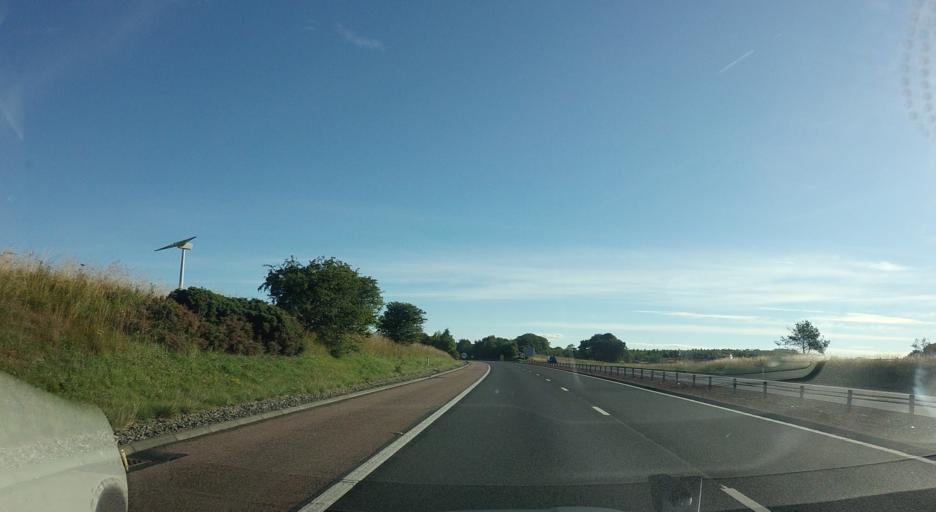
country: GB
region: Scotland
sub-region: Fife
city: Crossgates
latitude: 56.0997
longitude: -3.3923
